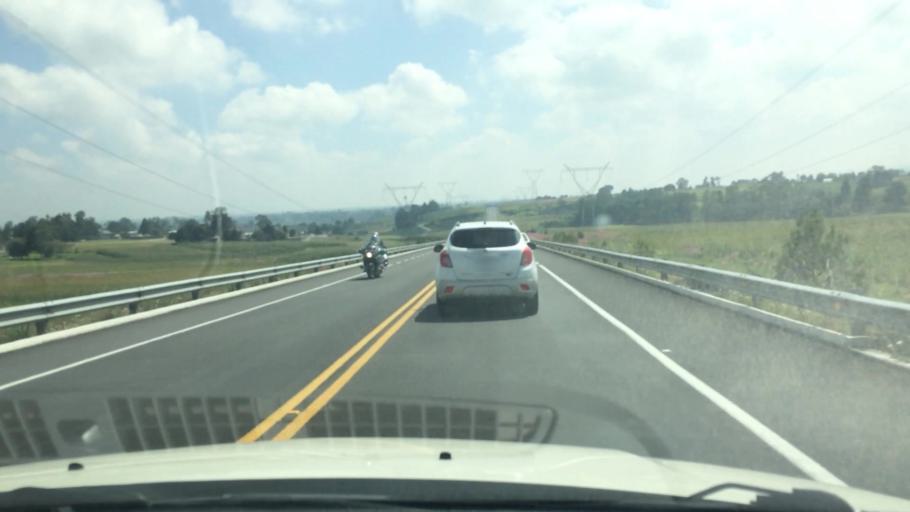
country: MX
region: Mexico
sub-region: Almoloya de Juarez
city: San Pedro de la Hortaliza (Ejido Almoloyan)
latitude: 19.3779
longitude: -99.8432
